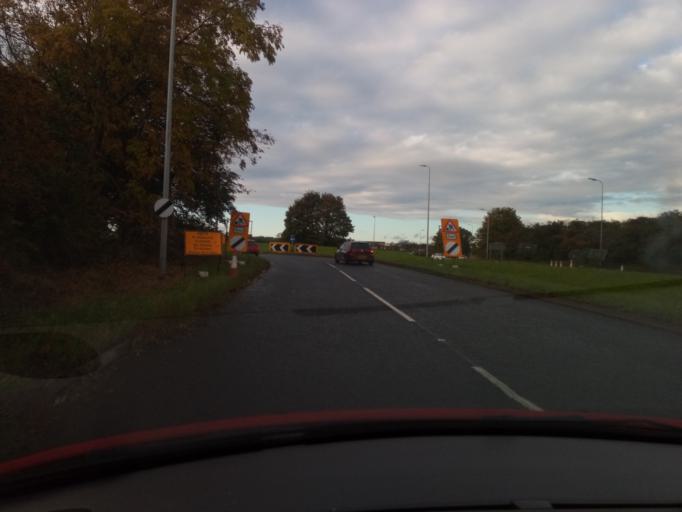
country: GB
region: England
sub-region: Darlington
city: Heighington
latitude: 54.5761
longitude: -1.6126
